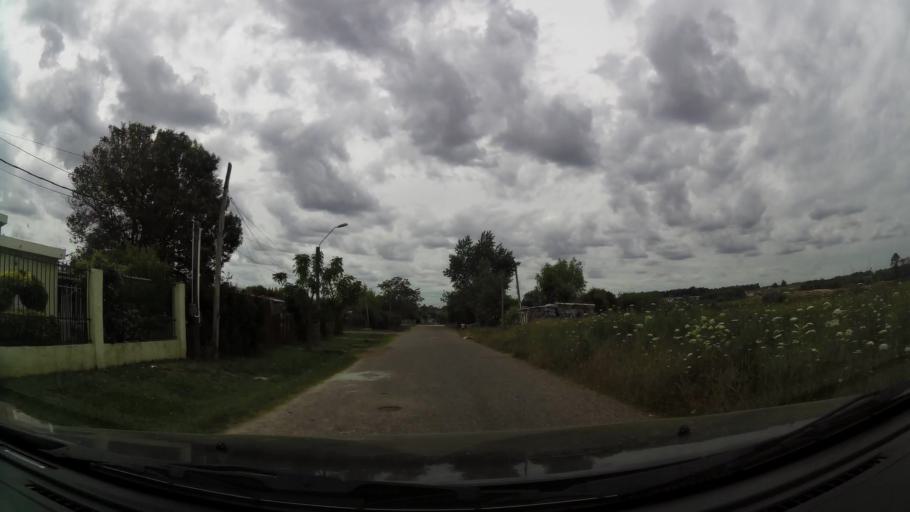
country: UY
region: Canelones
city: Las Piedras
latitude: -34.7158
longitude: -56.2078
